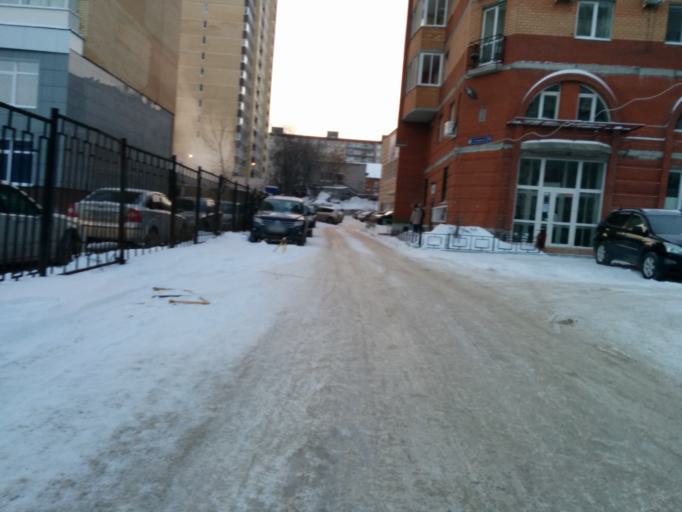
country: RU
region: Perm
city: Perm
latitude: 58.0039
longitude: 56.2672
